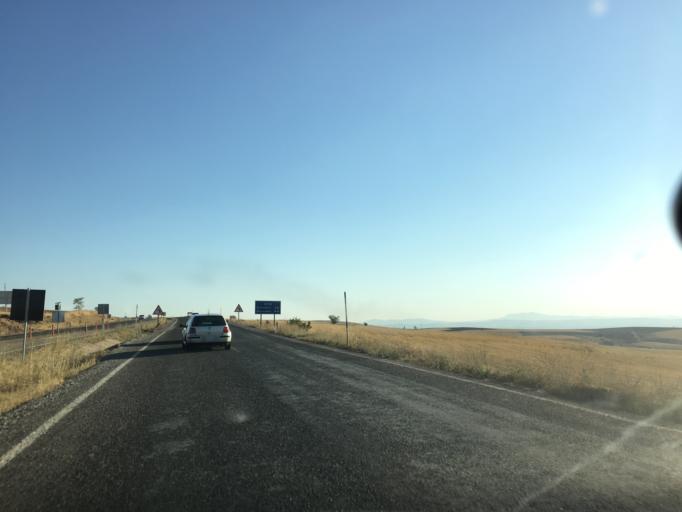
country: TR
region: Nevsehir
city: Hacibektas
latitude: 38.9233
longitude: 34.5458
